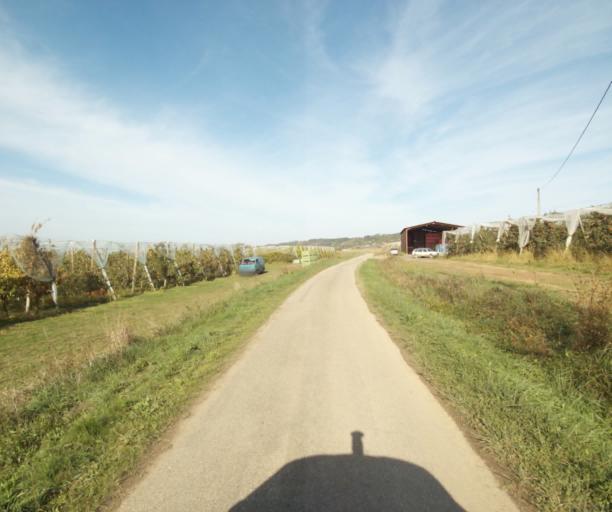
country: FR
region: Midi-Pyrenees
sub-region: Departement du Tarn-et-Garonne
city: Orgueil
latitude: 43.9150
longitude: 1.4342
